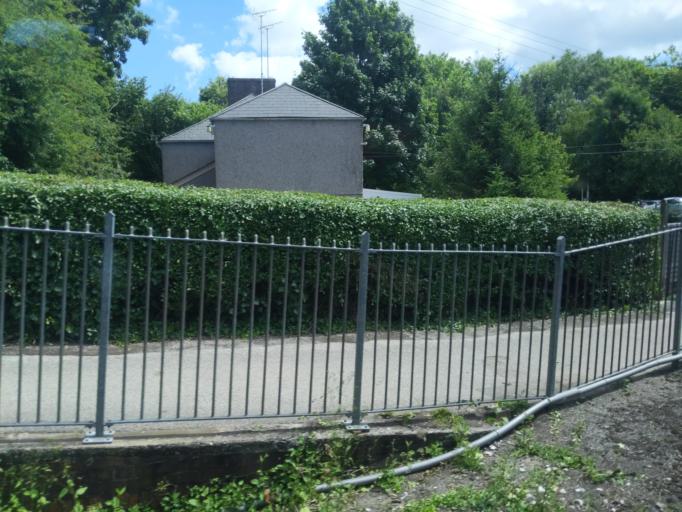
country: GB
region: England
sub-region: Cornwall
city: Par
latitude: 50.3566
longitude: -4.7046
